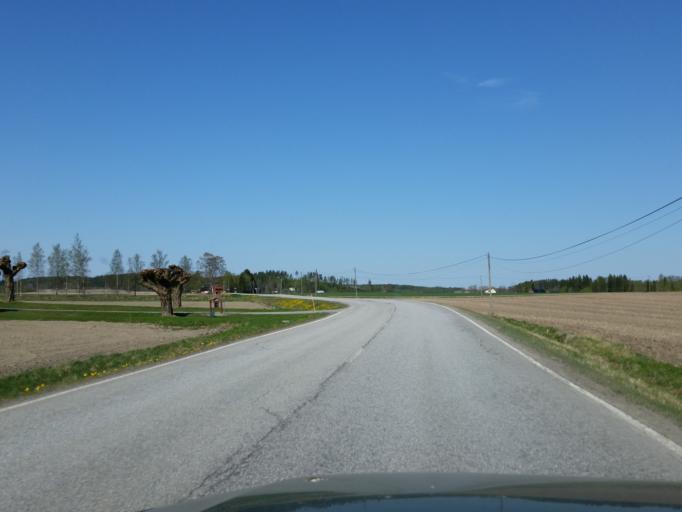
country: FI
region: Uusimaa
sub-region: Helsinki
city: Lohja
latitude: 60.1757
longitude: 24.0661
